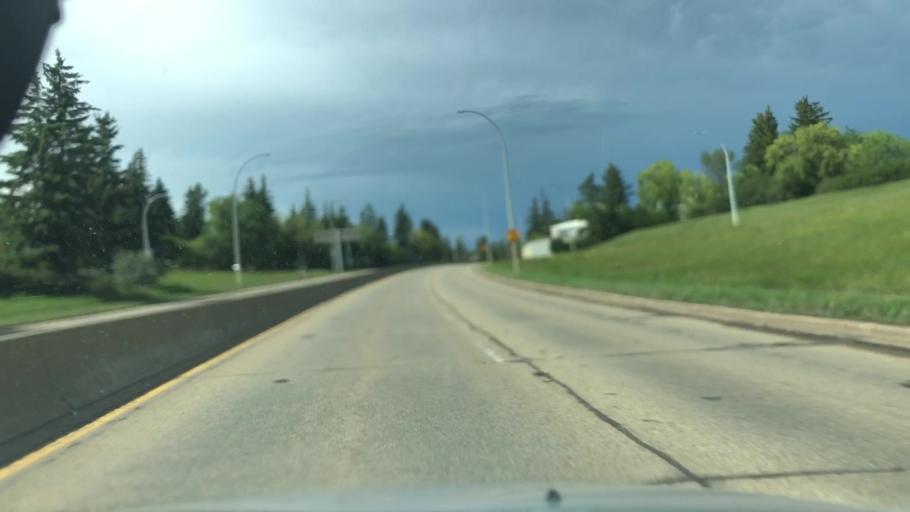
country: CA
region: Alberta
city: Edmonton
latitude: 53.5517
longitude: -113.5502
